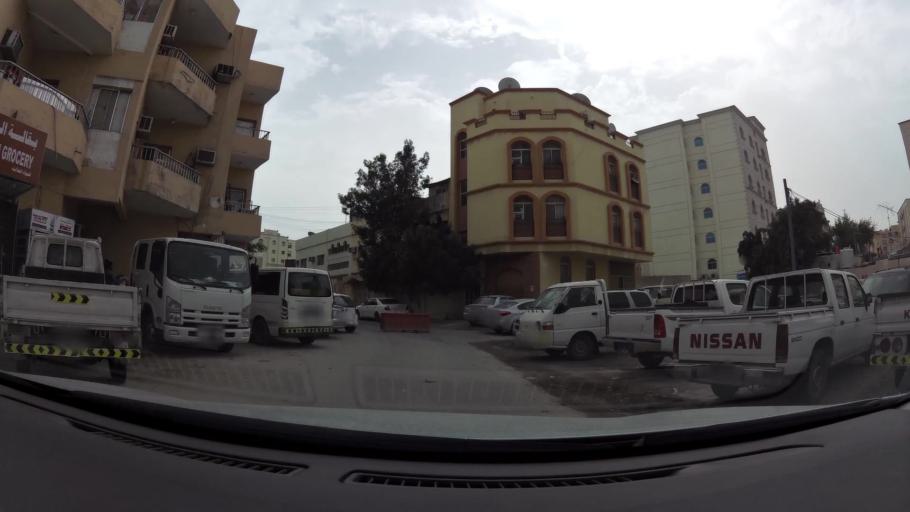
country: QA
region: Baladiyat ad Dawhah
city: Doha
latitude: 25.2674
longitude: 51.5402
